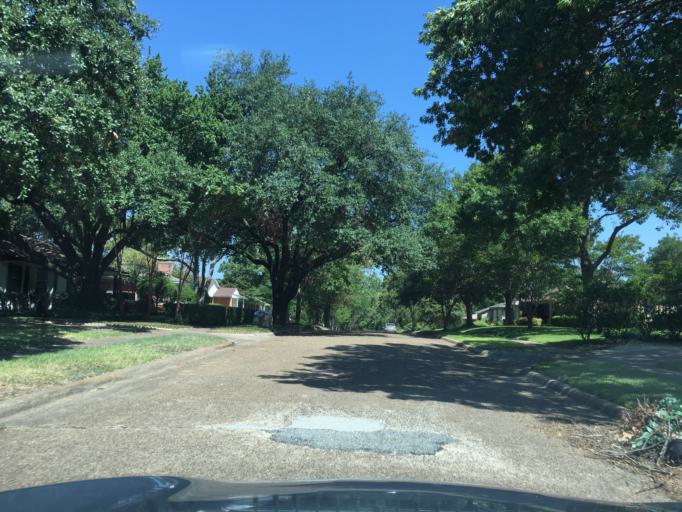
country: US
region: Texas
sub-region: Dallas County
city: Garland
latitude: 32.8535
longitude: -96.6911
